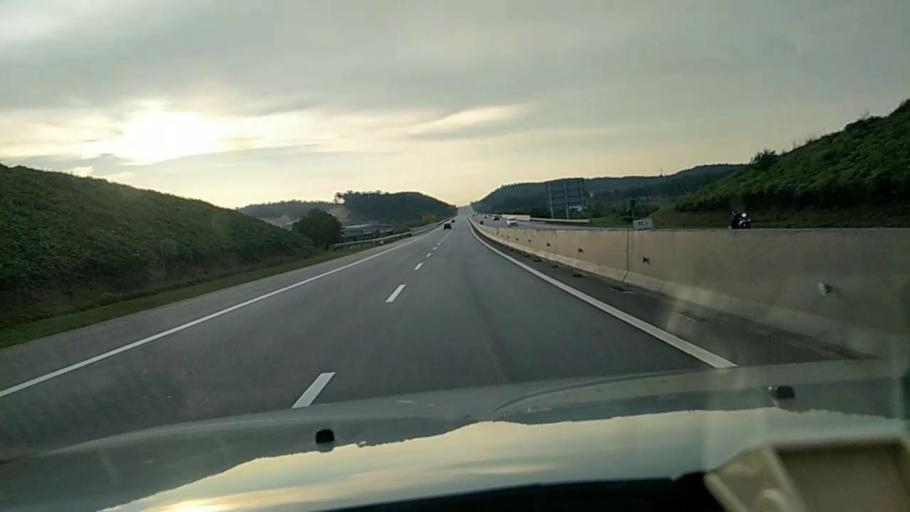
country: MY
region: Selangor
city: Batu Arang
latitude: 3.2748
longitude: 101.4562
